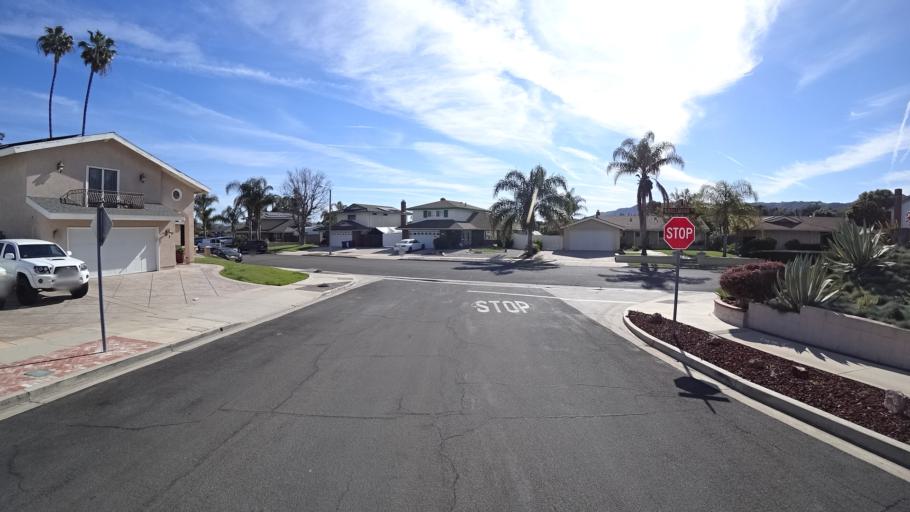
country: US
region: California
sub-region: Ventura County
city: Casa Conejo
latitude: 34.1753
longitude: -118.9575
